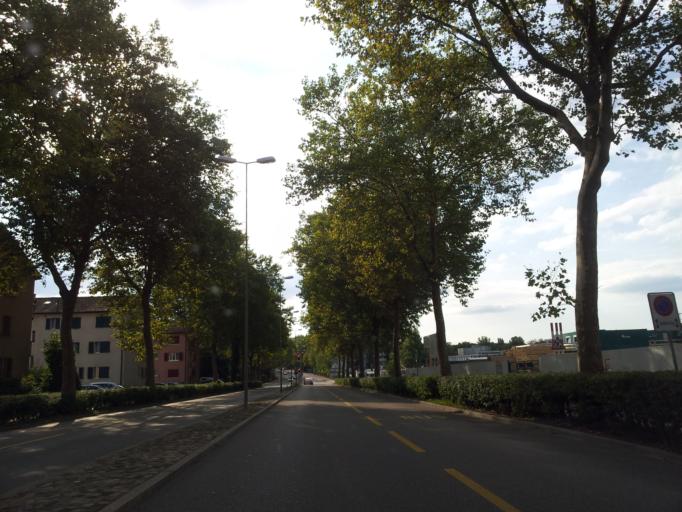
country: CH
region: Zurich
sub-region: Bezirk Dietikon
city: Schlieren / Spital
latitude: 47.3970
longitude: 8.4355
